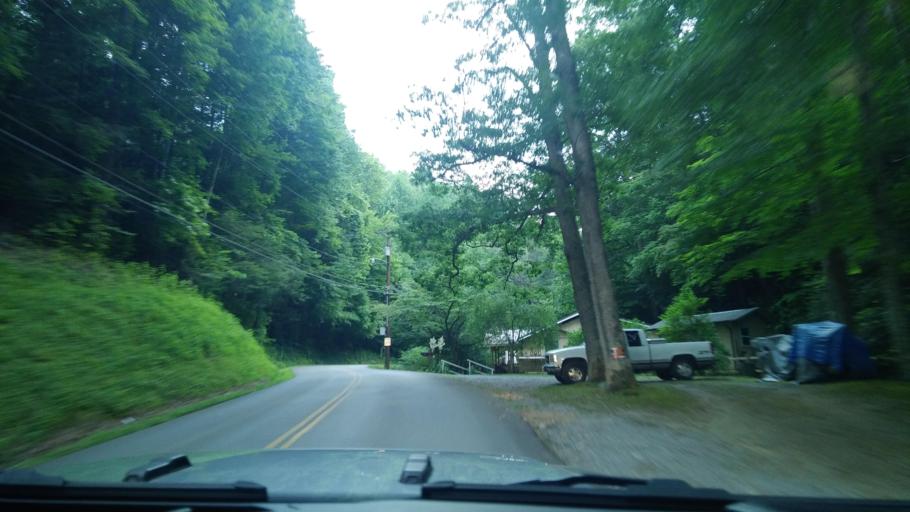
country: US
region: Tennessee
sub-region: Sevier County
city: Gatlinburg
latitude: 35.7273
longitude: -83.4899
